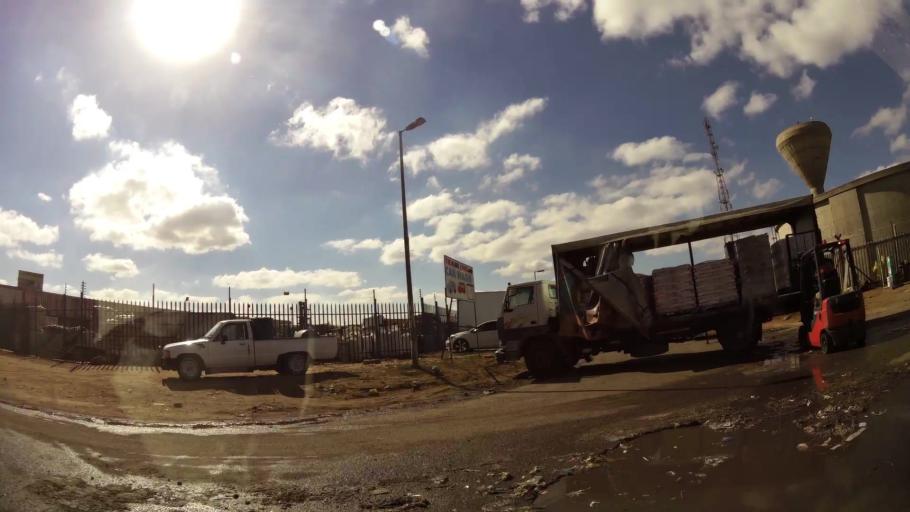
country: ZA
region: Gauteng
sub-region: City of Johannesburg Metropolitan Municipality
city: Modderfontein
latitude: -26.0322
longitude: 28.1749
